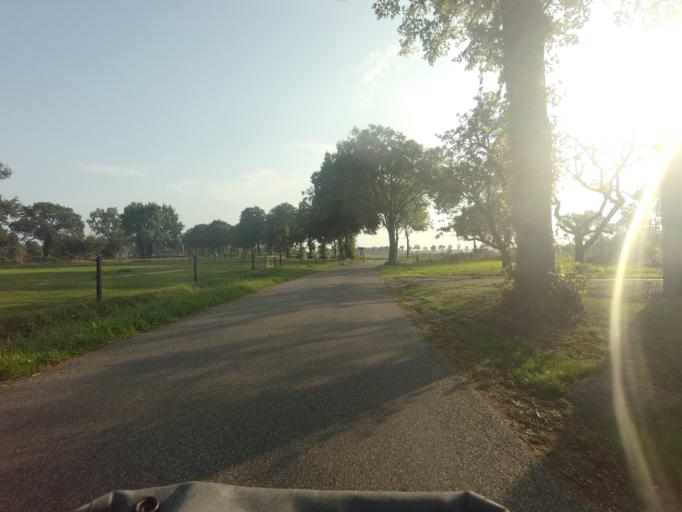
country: NL
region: Drenthe
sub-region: Gemeente Tynaarlo
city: Vries
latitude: 53.1130
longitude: 6.5236
